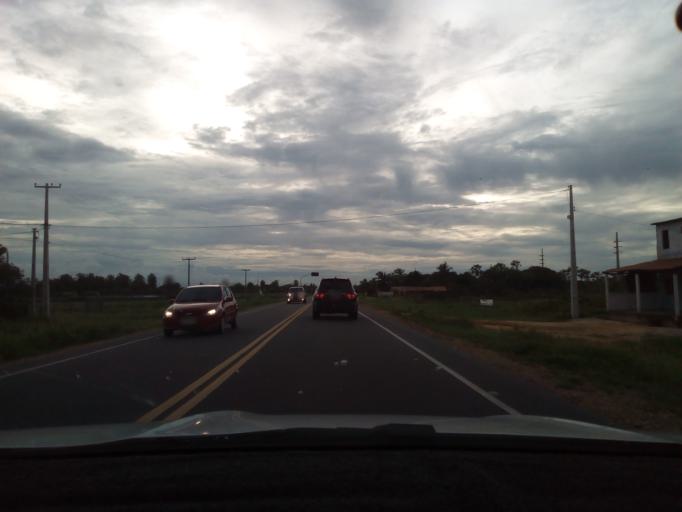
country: BR
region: Ceara
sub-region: Aracati
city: Aracati
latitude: -4.3742
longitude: -37.9269
